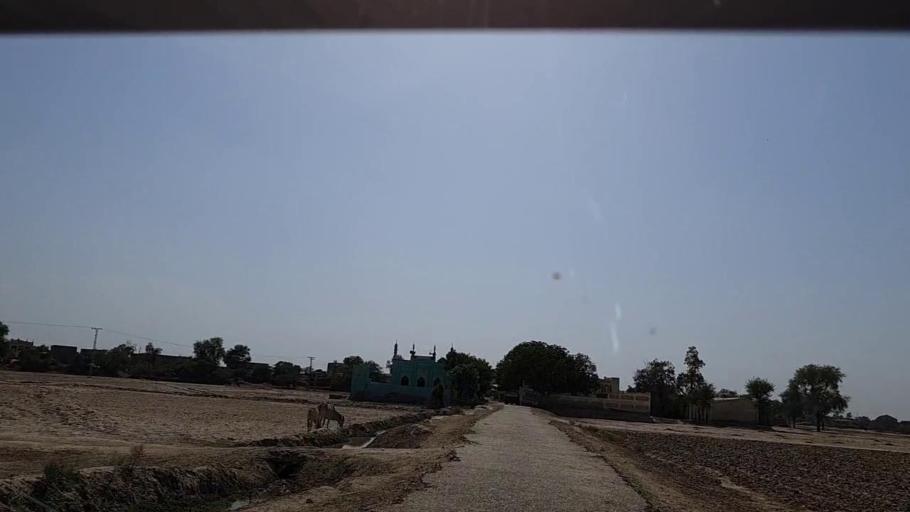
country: PK
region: Sindh
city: Phulji
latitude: 26.9510
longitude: 67.6822
